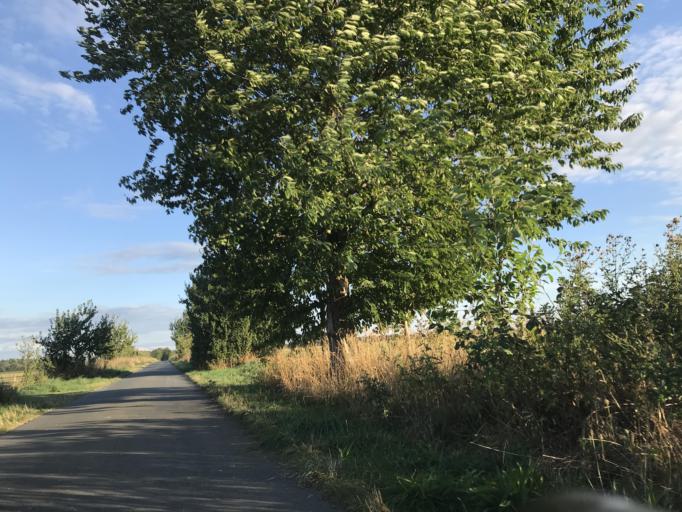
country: DE
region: Lower Saxony
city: Reinstorf
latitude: 53.2386
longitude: 10.5874
